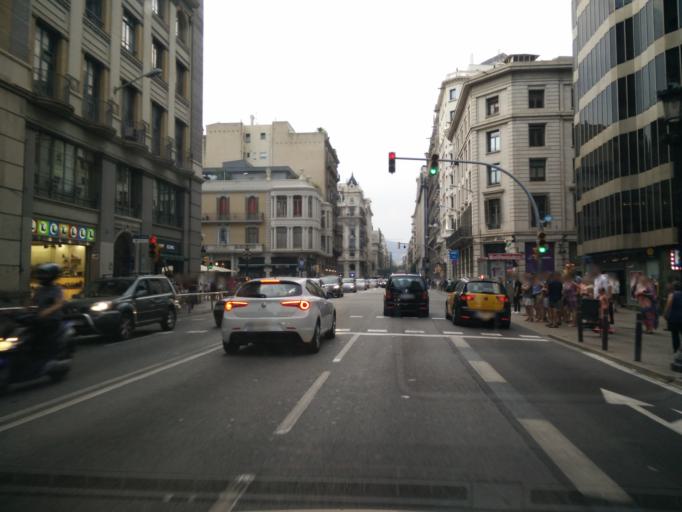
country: ES
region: Catalonia
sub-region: Provincia de Barcelona
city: Ciutat Vella
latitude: 41.3837
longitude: 2.1792
